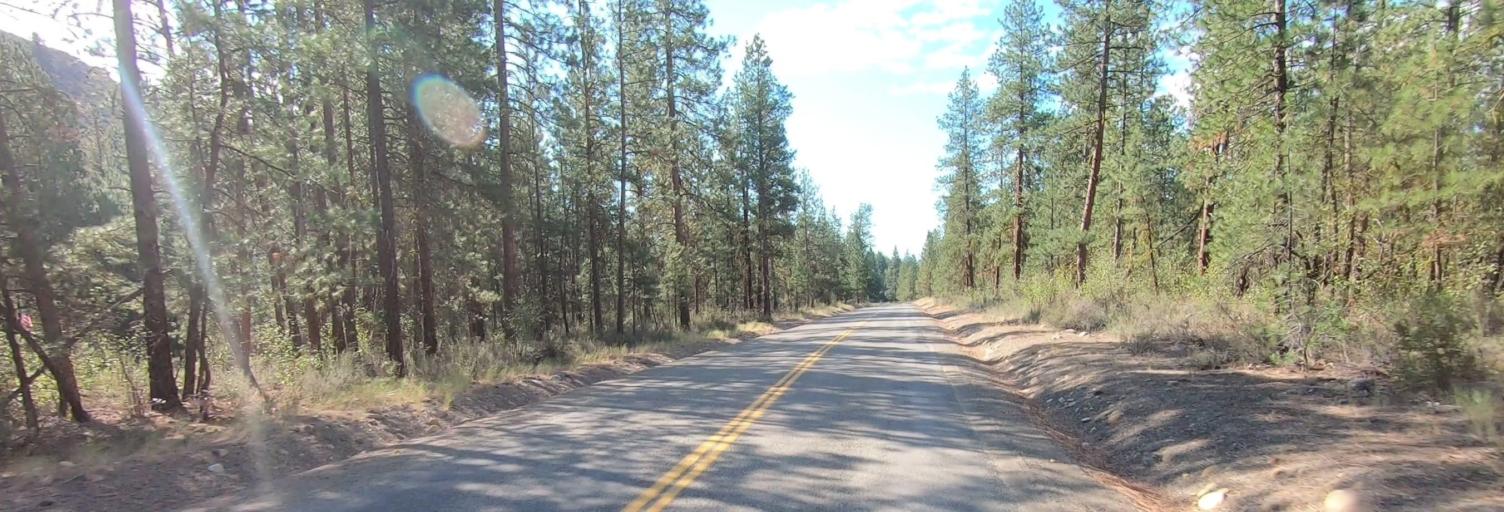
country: US
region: Washington
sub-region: Okanogan County
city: Brewster
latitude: 48.5355
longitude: -120.1789
